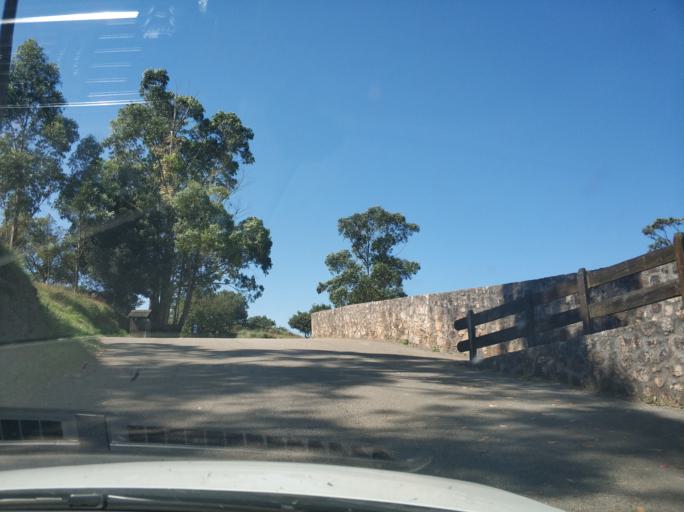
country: ES
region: Cantabria
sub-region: Provincia de Cantabria
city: Penagos
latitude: 43.3640
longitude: -3.8378
